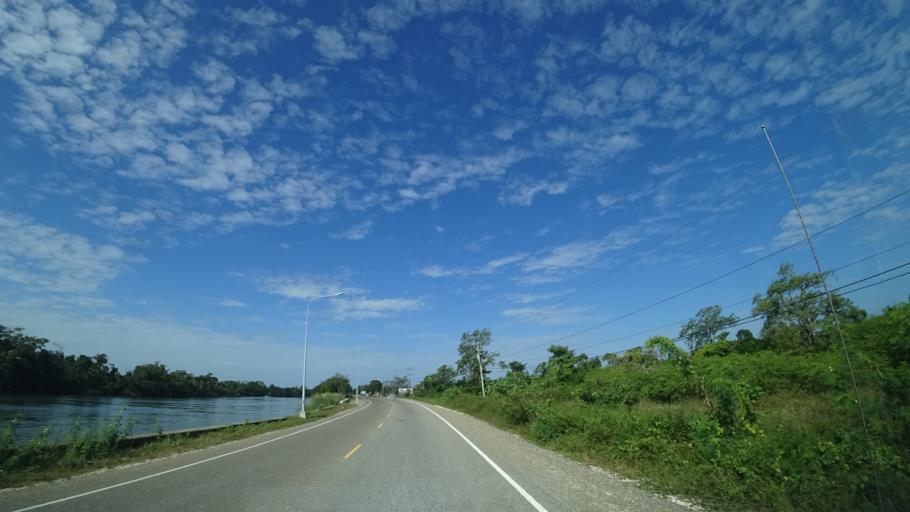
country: BZ
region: Belize
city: Belize City
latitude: 17.5442
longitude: -88.2675
